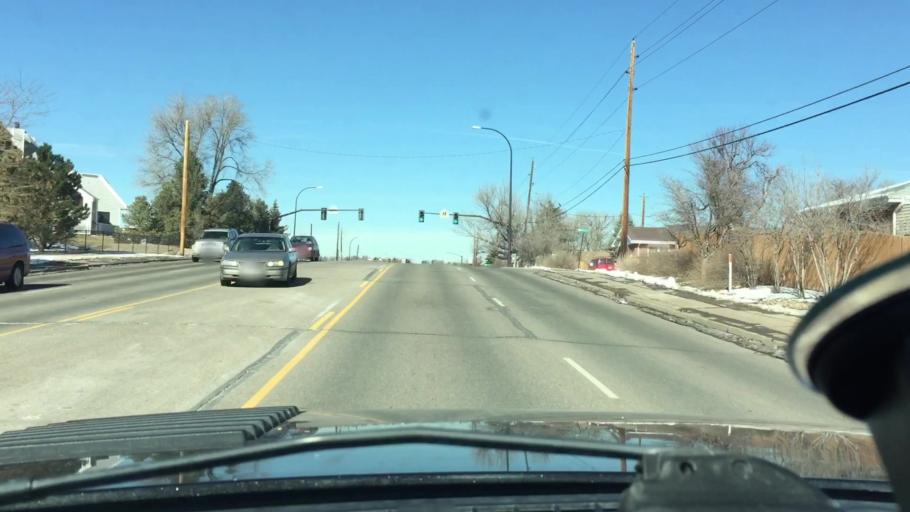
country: US
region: Colorado
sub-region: Adams County
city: Federal Heights
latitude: 39.8542
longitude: -104.9966
